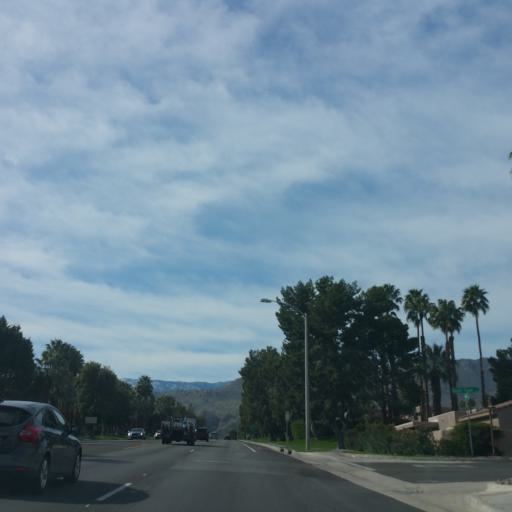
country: US
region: California
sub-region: Riverside County
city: Palm Desert
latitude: 33.6984
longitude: -116.3992
